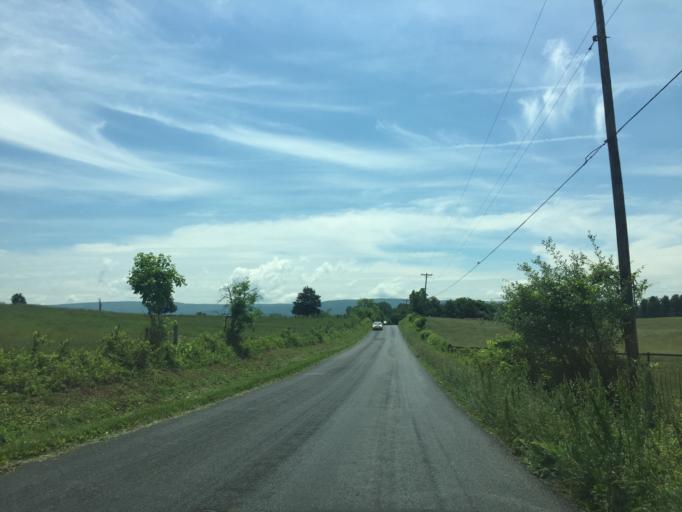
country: US
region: Virginia
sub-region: Warren County
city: Shenandoah Farms
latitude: 38.9876
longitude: -78.1389
